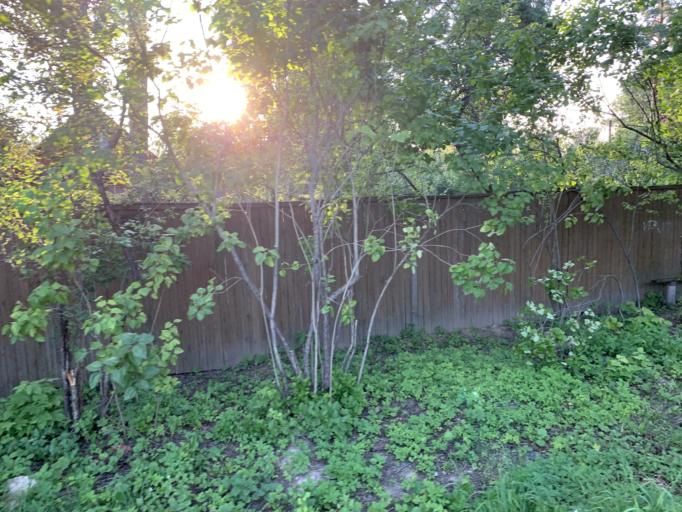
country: RU
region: Moskovskaya
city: Lesnyye Polyany
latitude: 55.9739
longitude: 37.8460
